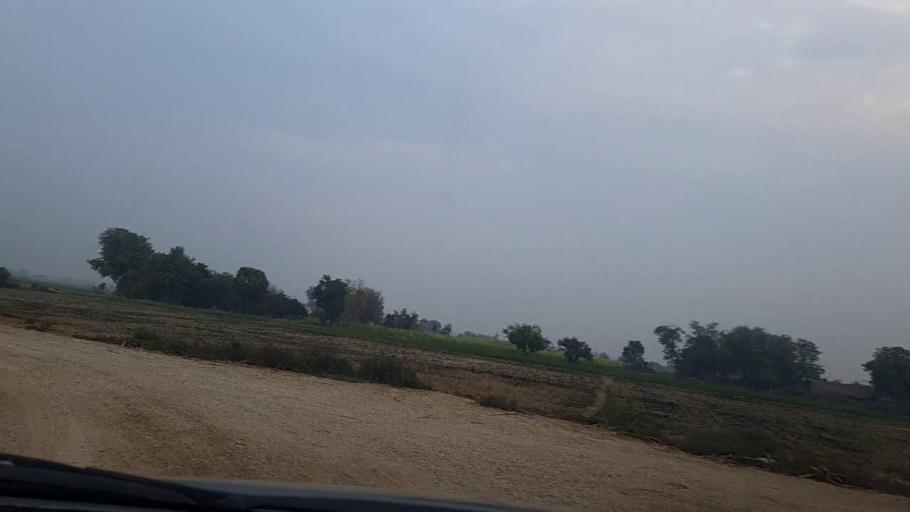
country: PK
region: Sindh
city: Sakrand
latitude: 26.2902
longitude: 68.2439
